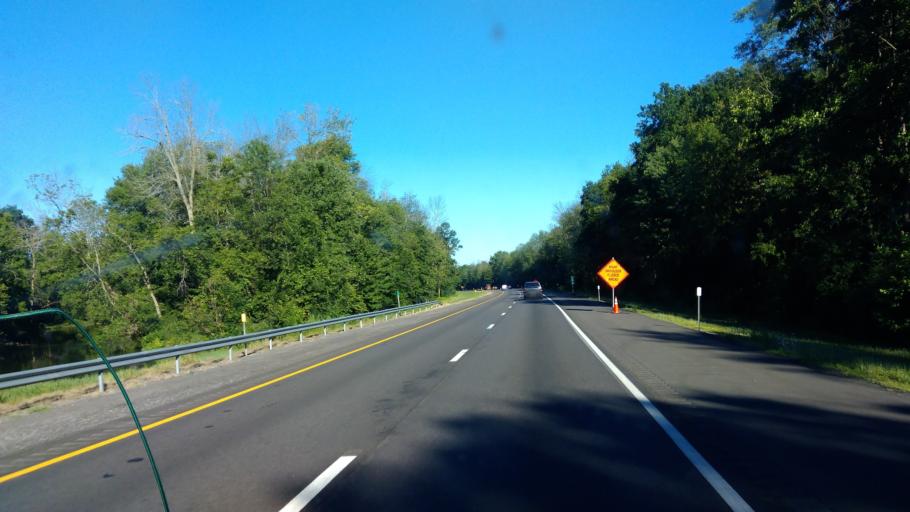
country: US
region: New York
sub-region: Ontario County
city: Shortsville
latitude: 42.9761
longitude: -77.1891
